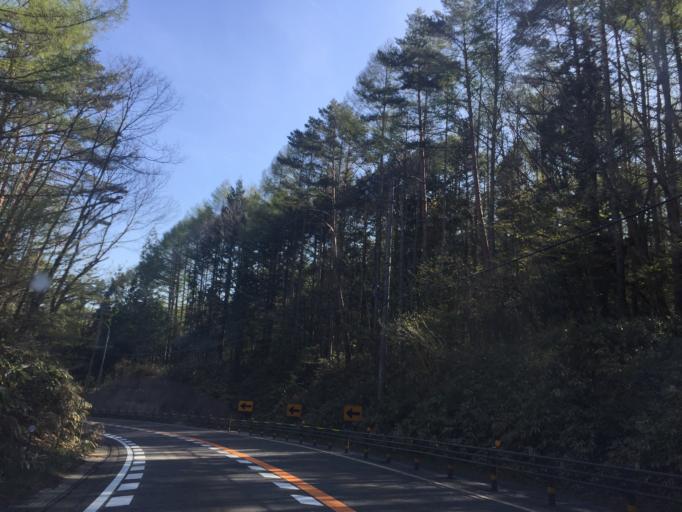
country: JP
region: Gifu
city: Nakatsugawa
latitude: 35.3597
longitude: 137.6725
